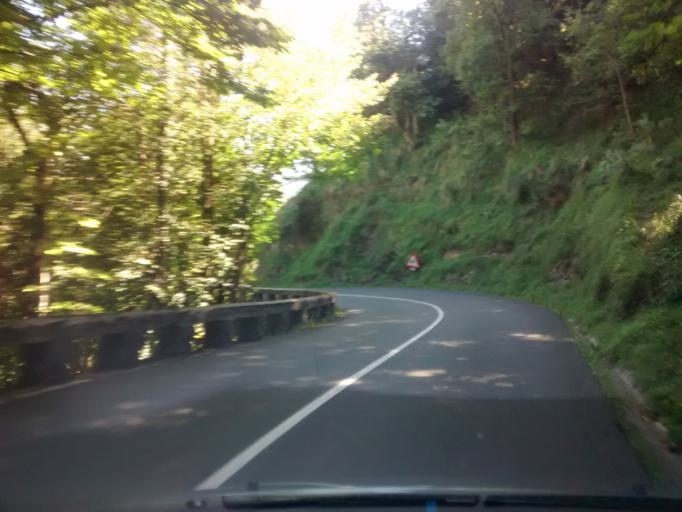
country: ES
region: Basque Country
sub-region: Provincia de Guipuzcoa
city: Eibar
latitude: 43.1988
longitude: -2.4765
